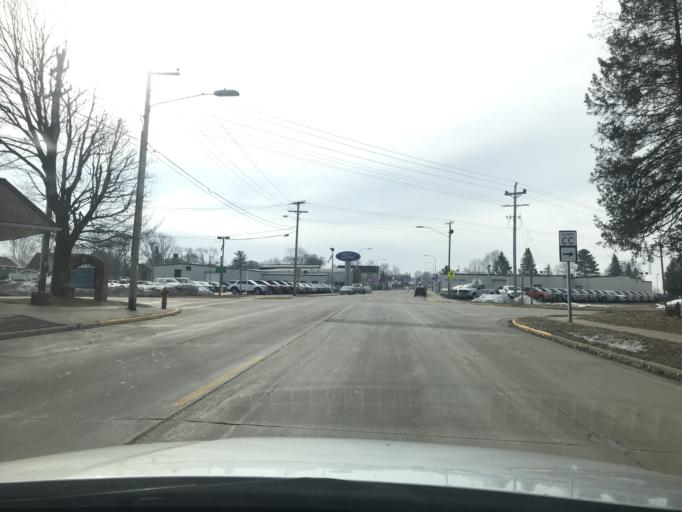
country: US
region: Wisconsin
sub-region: Oconto County
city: Oconto Falls
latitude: 44.8782
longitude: -88.1468
